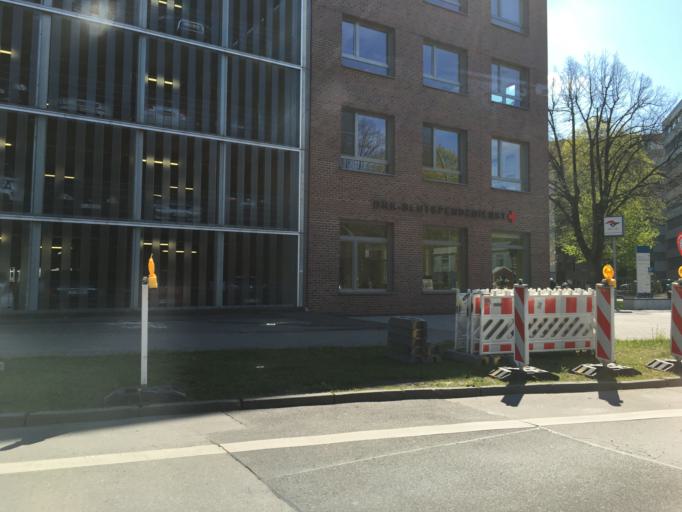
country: DE
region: Brandenburg
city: Potsdam
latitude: 52.4017
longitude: 13.0632
